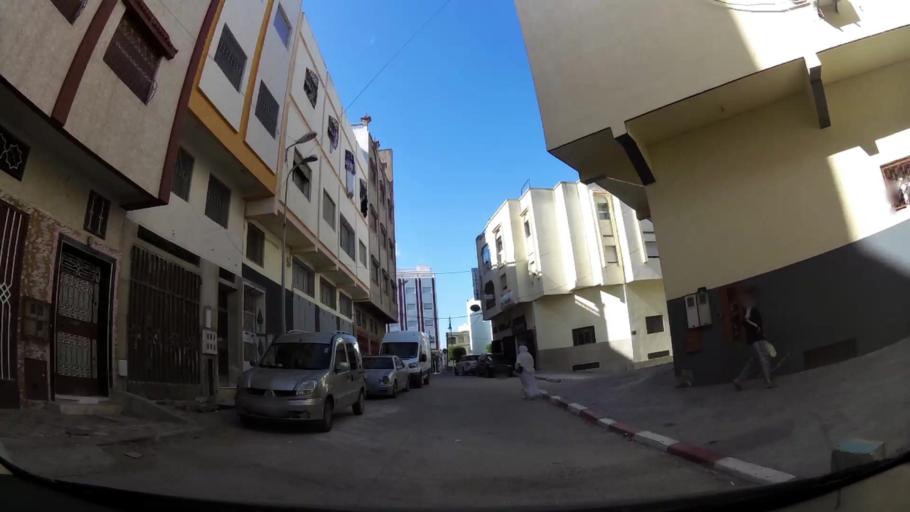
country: MA
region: Tanger-Tetouan
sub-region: Tanger-Assilah
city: Tangier
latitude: 35.7478
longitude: -5.8080
